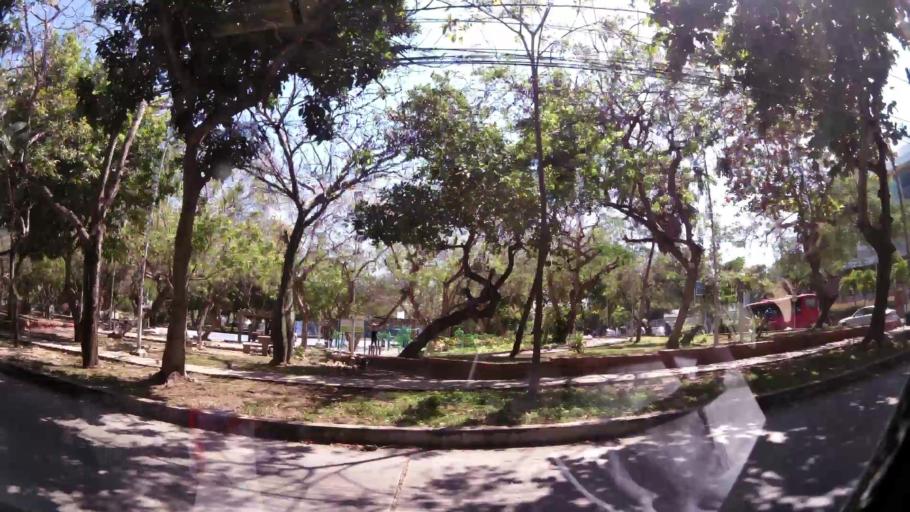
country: CO
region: Atlantico
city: Barranquilla
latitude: 11.0106
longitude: -74.8084
